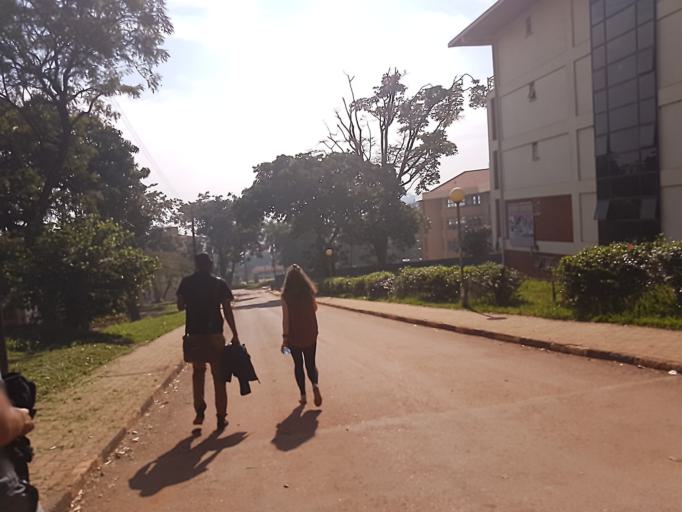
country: UG
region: Central Region
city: Kampala Central Division
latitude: 0.3354
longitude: 32.5673
